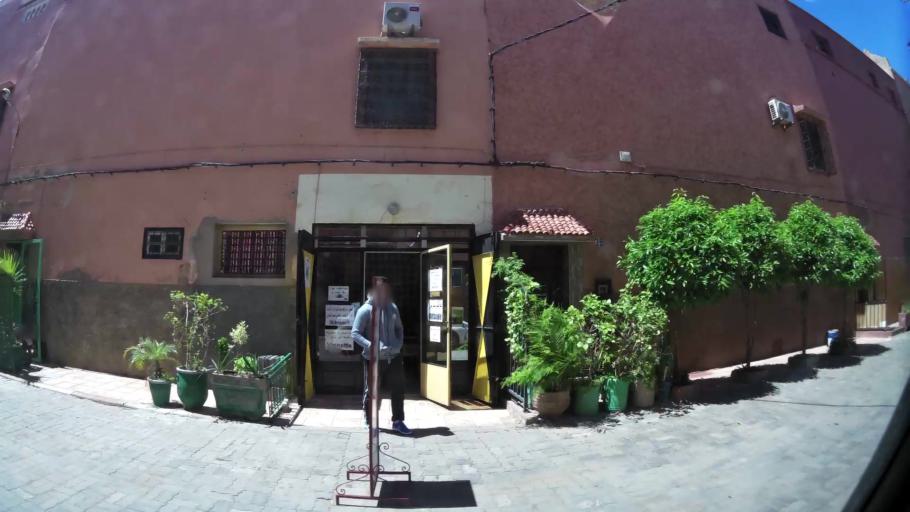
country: MA
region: Marrakech-Tensift-Al Haouz
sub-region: Marrakech
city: Marrakesh
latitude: 31.6469
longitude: -7.9937
